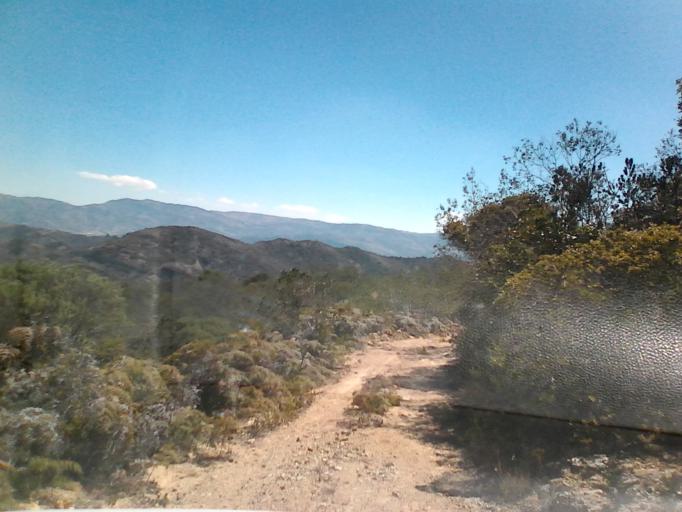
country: CO
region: Boyaca
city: Sachica
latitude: 5.5301
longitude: -73.5434
